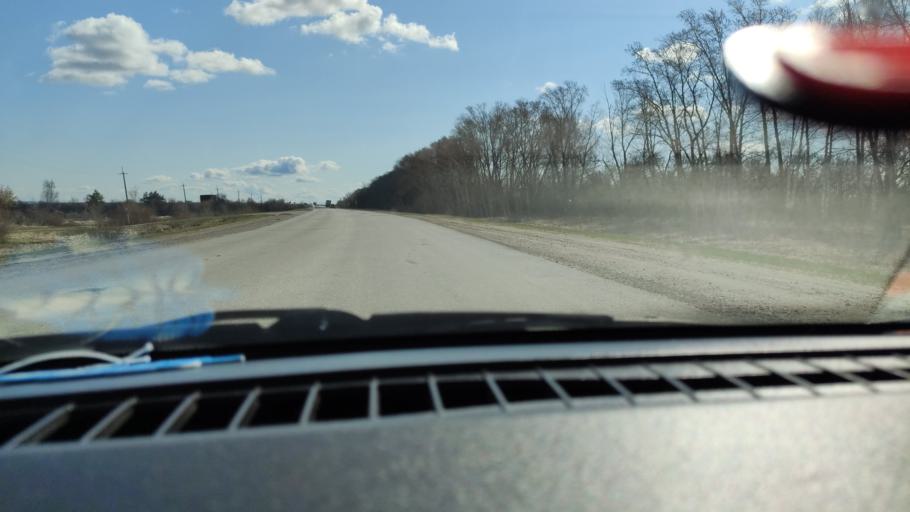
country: RU
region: Samara
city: Varlamovo
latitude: 53.1223
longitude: 48.3100
